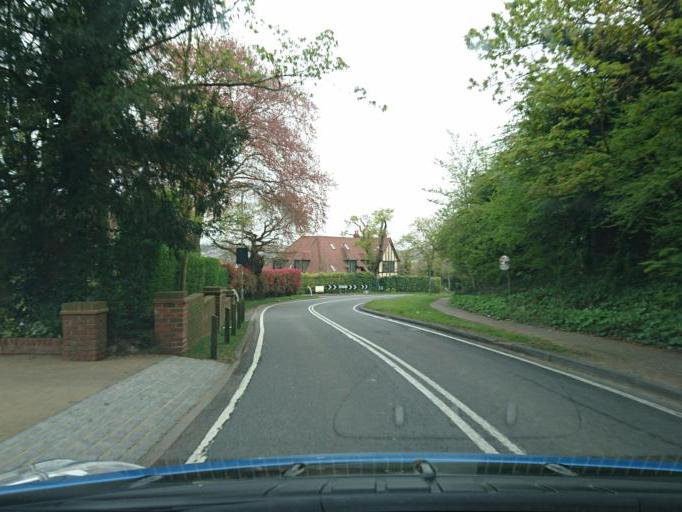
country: GB
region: England
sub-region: Greater London
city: Barnet
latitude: 51.6366
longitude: -0.1982
